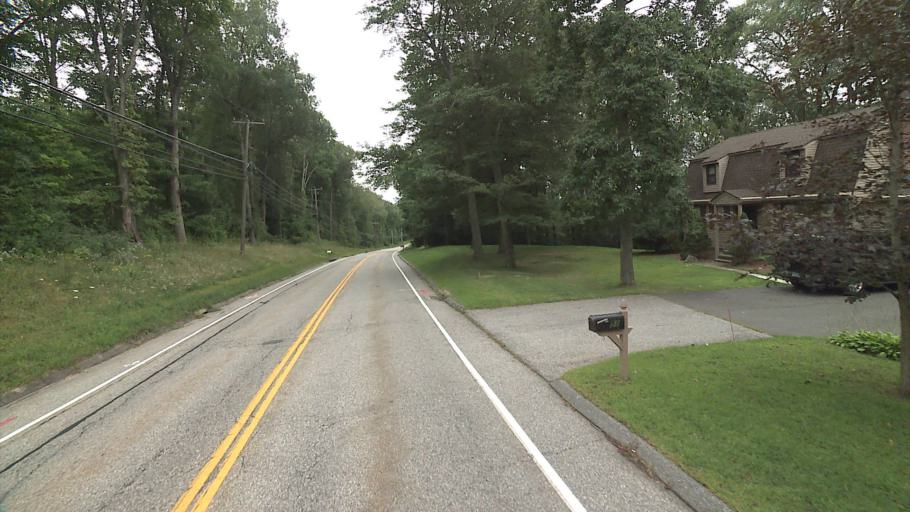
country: US
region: Connecticut
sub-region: Hartford County
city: Manchester
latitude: 41.7641
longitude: -72.4419
